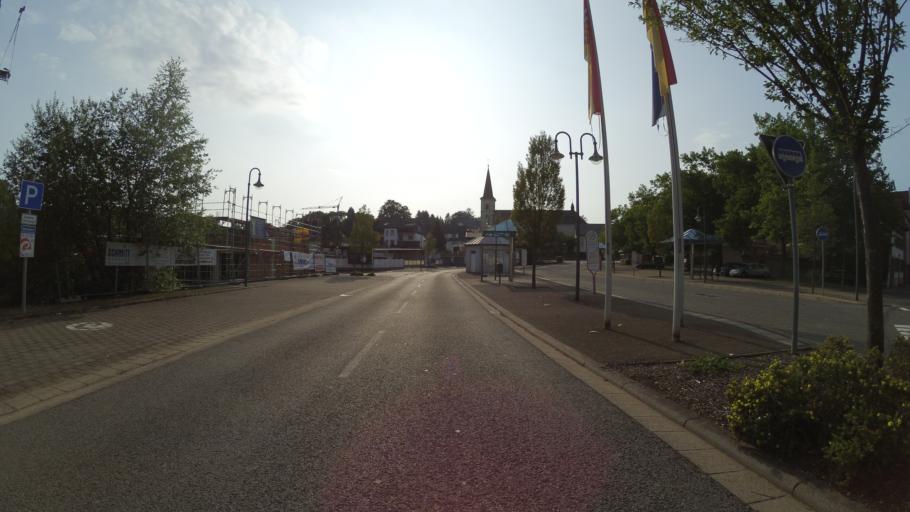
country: DE
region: Saarland
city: Wadern
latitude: 49.5388
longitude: 6.8927
